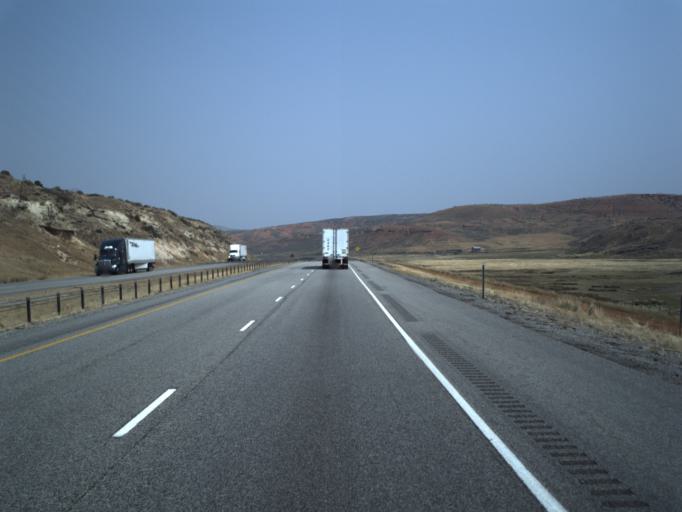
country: US
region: Wyoming
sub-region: Uinta County
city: Evanston
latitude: 41.1263
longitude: -111.1661
